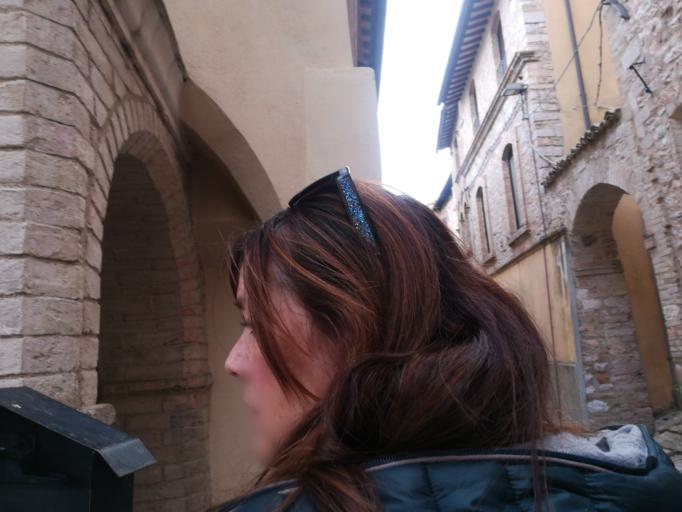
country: IT
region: Umbria
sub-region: Provincia di Perugia
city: Spello
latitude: 42.9948
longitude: 12.6723
